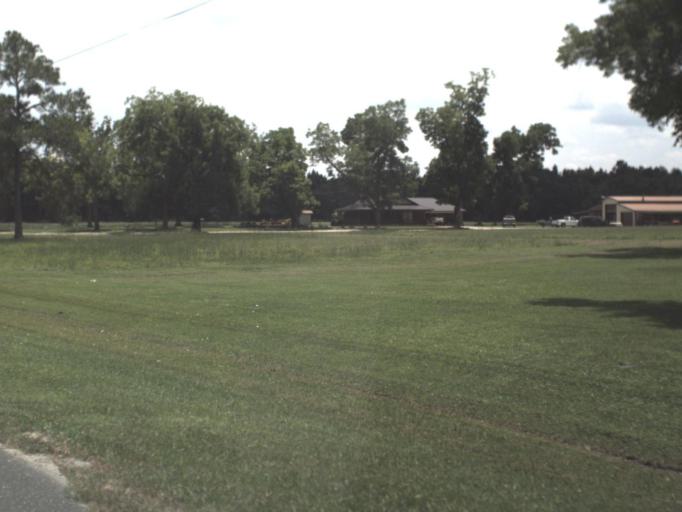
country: US
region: Florida
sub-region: Bradford County
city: Starke
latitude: 30.0338
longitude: -82.1616
